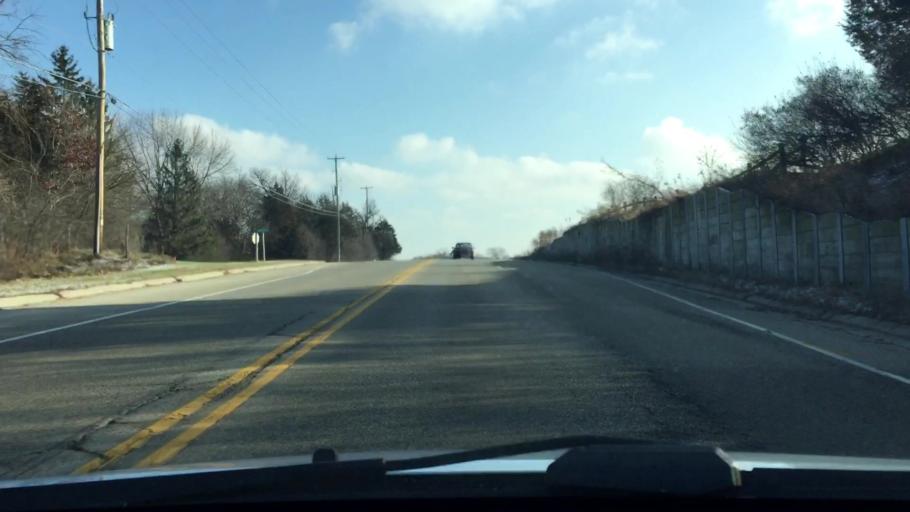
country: US
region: Wisconsin
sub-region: Waukesha County
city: Dousman
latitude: 43.0216
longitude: -88.4548
